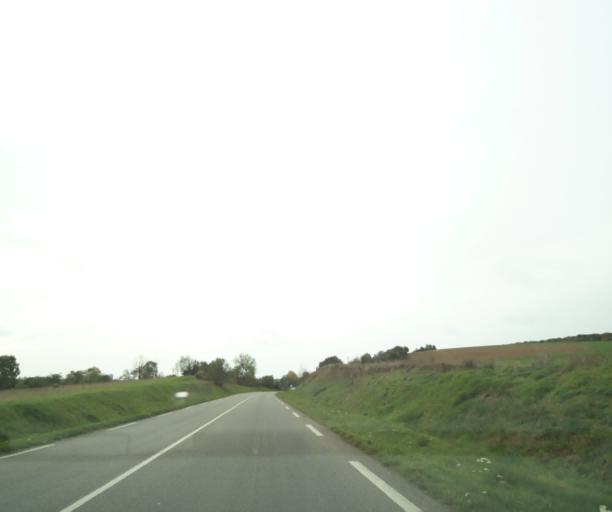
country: FR
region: Centre
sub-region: Departement d'Eure-et-Loir
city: Luray
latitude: 48.7581
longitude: 1.3964
